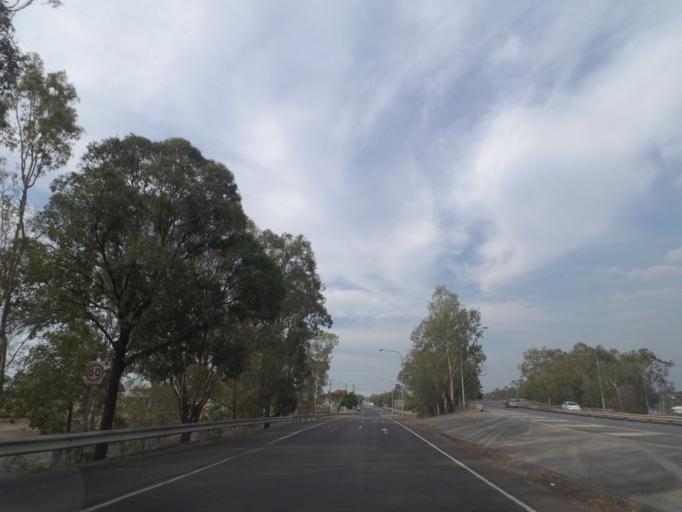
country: AU
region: Queensland
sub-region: Brisbane
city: Rocklea
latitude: -27.5450
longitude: 153.0104
